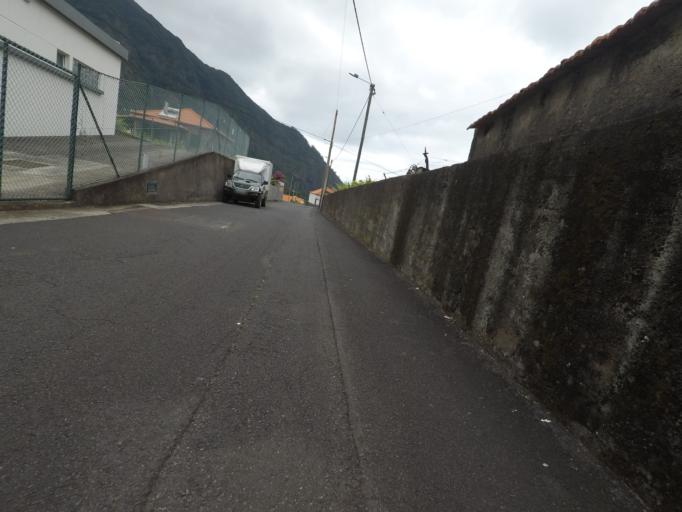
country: PT
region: Madeira
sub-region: Sao Vicente
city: Sao Vicente
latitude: 32.7899
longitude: -17.0367
